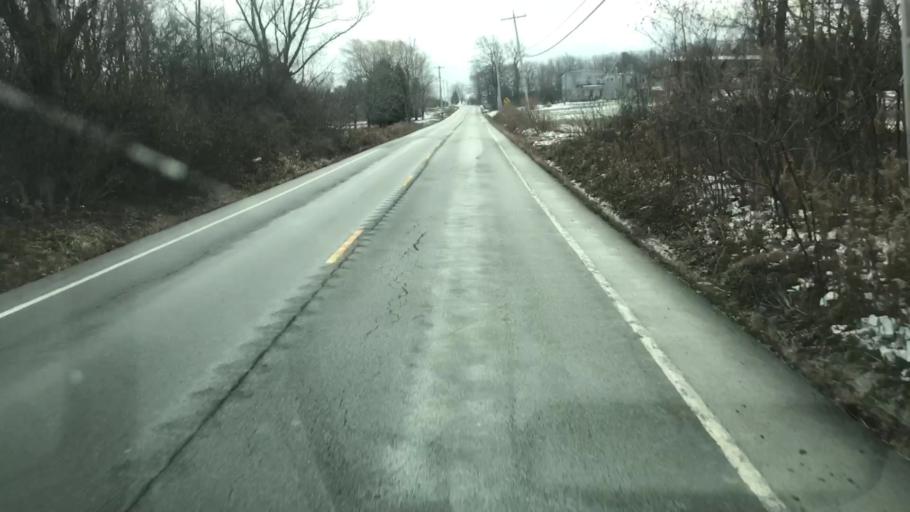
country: US
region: New York
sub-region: Onondaga County
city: Skaneateles
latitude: 42.8516
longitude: -76.3938
